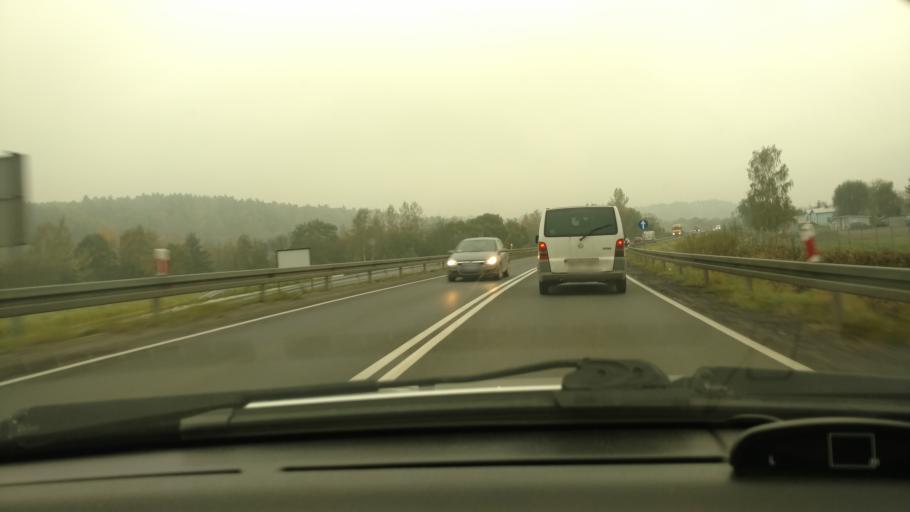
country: PL
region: Lesser Poland Voivodeship
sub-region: Powiat gorlicki
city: Kobylanka
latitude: 49.6753
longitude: 21.1902
